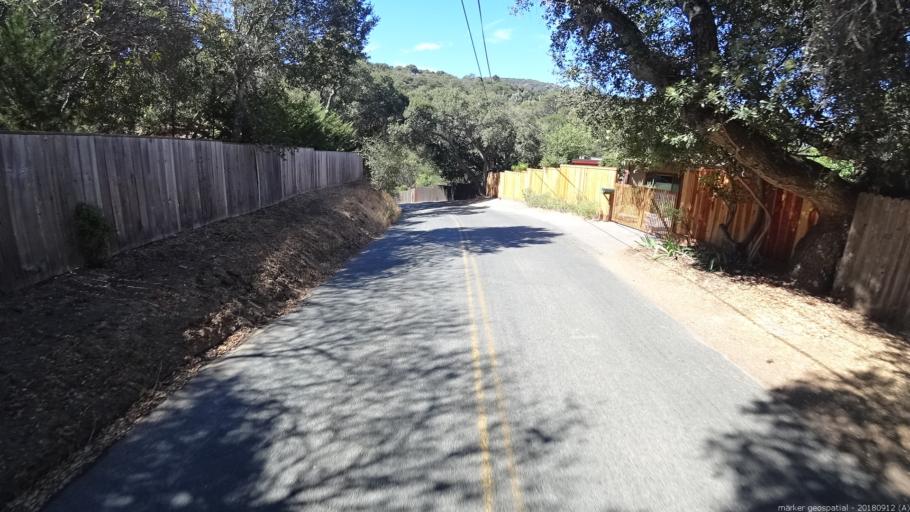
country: US
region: California
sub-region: Monterey County
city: Carmel Valley Village
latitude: 36.4718
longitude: -121.7238
